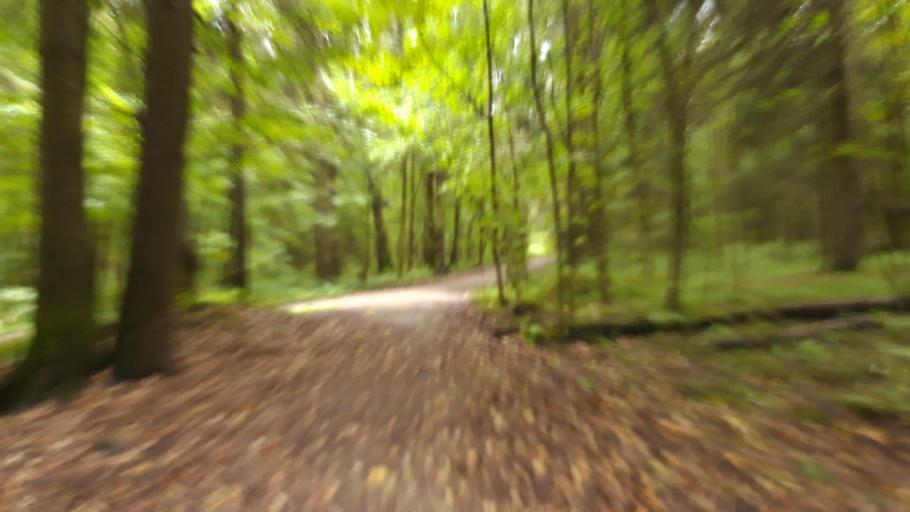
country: RU
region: Moscow
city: Zelenograd
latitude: 55.9863
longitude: 37.2032
